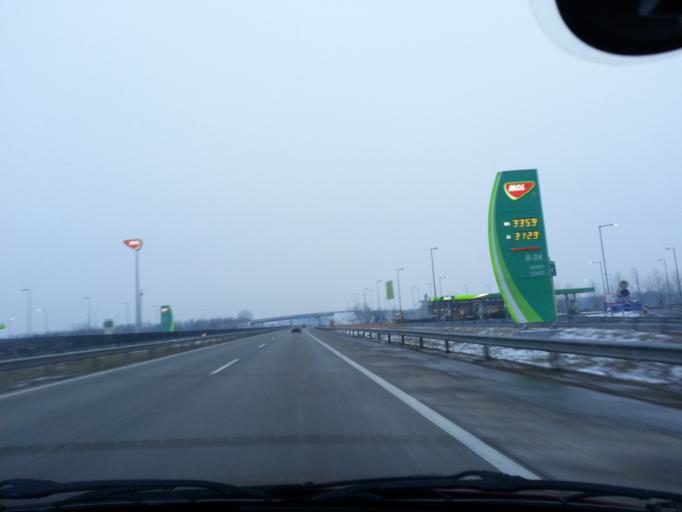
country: HU
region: Pest
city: Vecses
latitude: 47.3850
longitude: 19.2841
